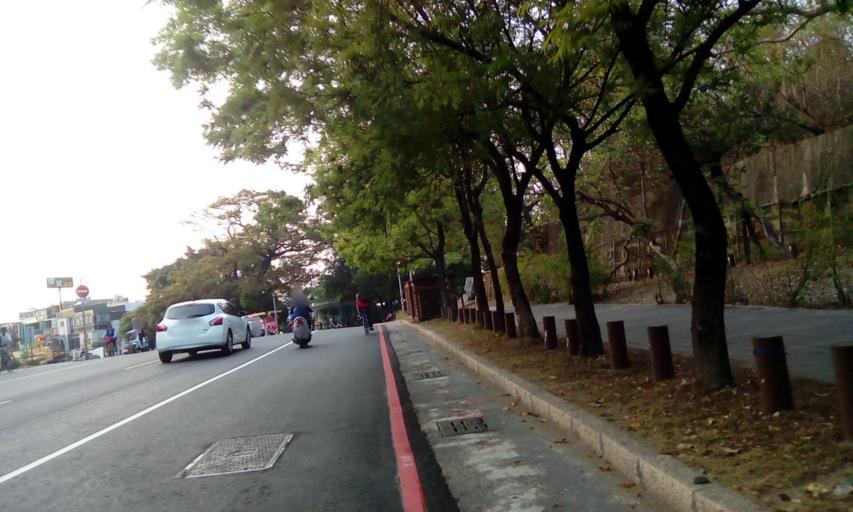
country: TW
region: Kaohsiung
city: Kaohsiung
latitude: 22.6792
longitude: 120.2925
